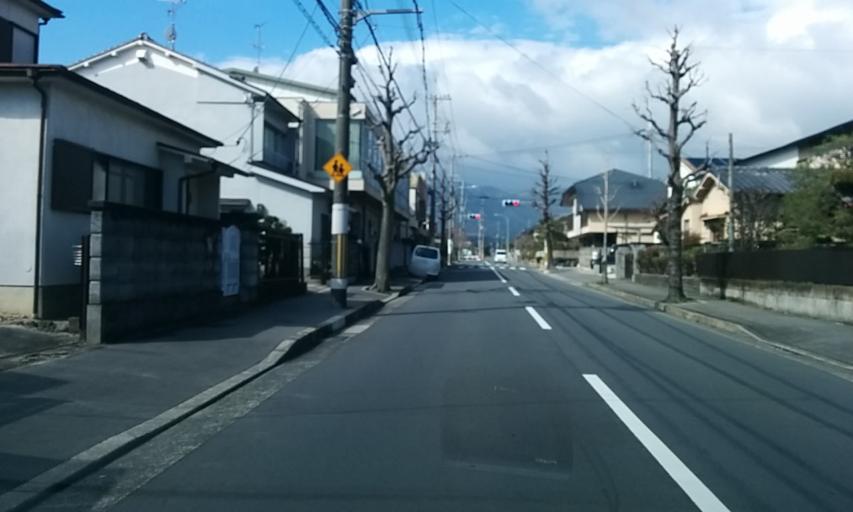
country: JP
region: Kyoto
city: Muko
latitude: 34.9473
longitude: 135.6894
